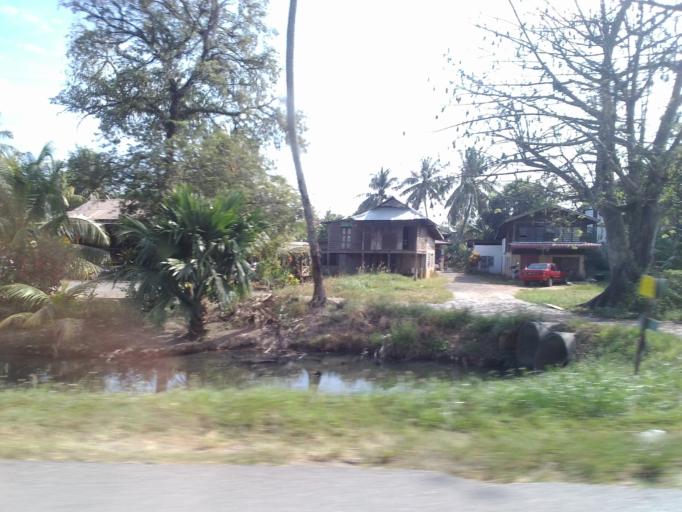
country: MY
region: Kedah
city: Gurun
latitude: 5.9604
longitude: 100.4051
